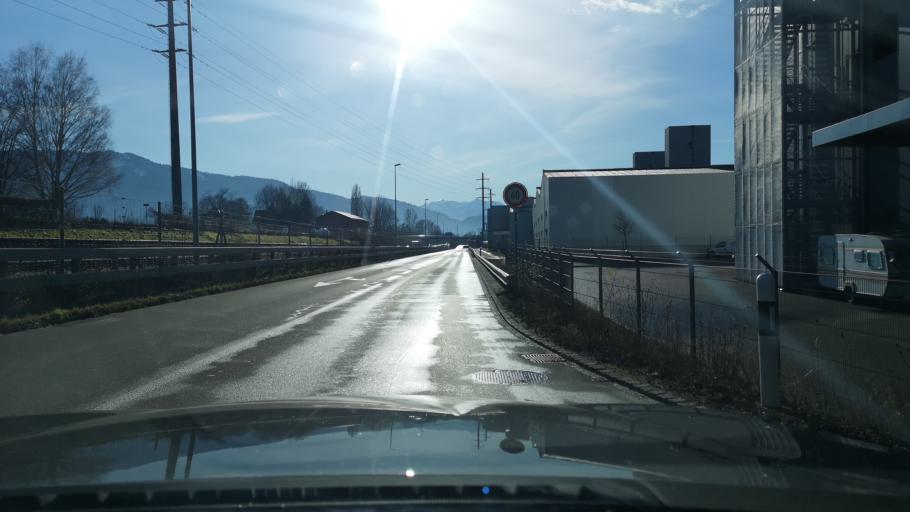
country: AT
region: Vorarlberg
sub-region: Politischer Bezirk Dornbirn
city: Lustenau
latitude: 47.4119
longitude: 9.6475
